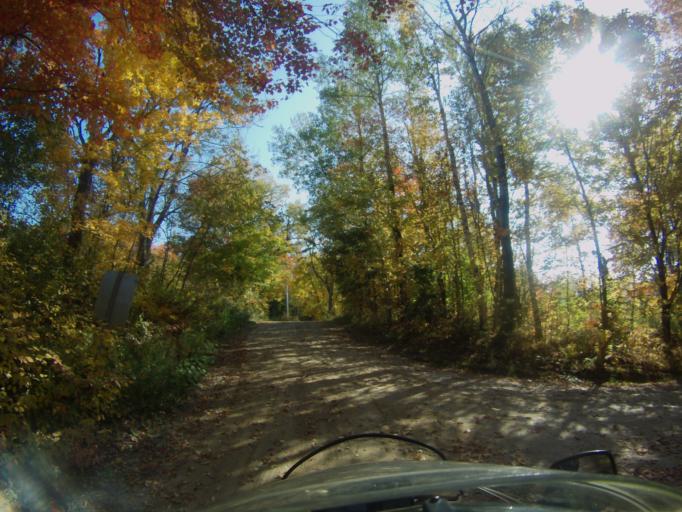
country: US
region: Vermont
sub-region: Addison County
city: Bristol
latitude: 44.0991
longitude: -72.9744
